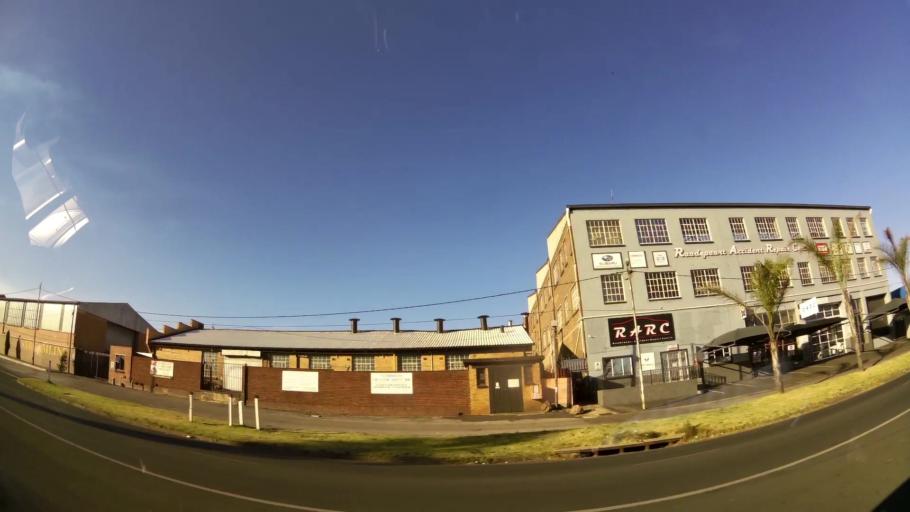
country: ZA
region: Gauteng
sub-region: City of Johannesburg Metropolitan Municipality
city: Roodepoort
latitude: -26.1456
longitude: 27.8620
